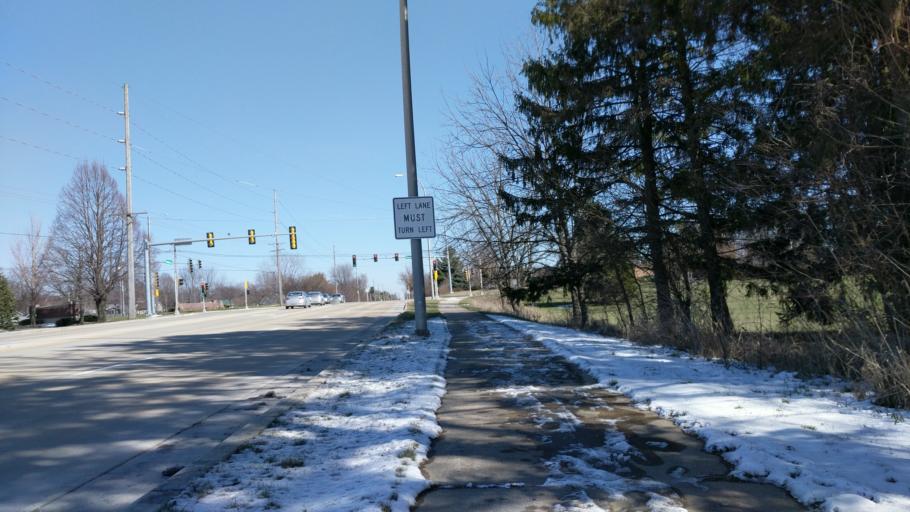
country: US
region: Illinois
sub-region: Champaign County
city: Urbana
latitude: 40.0836
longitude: -88.2106
